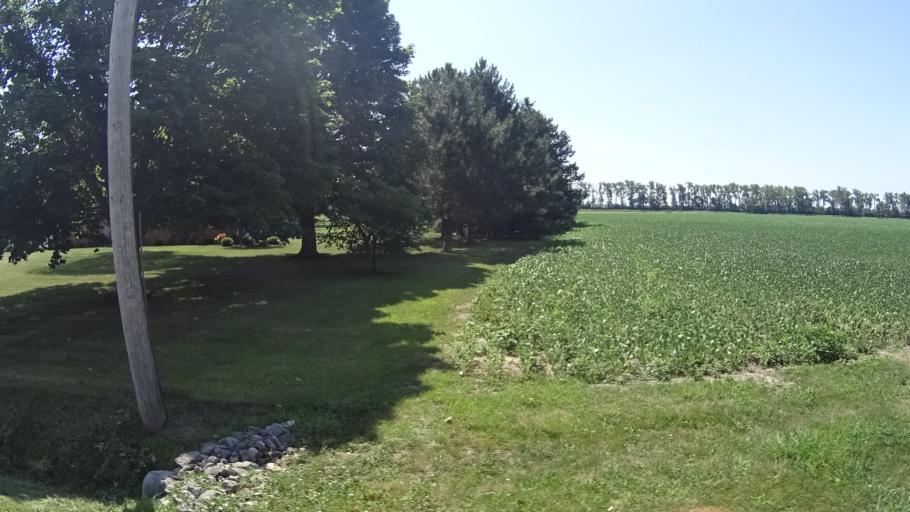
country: US
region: Ohio
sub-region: Erie County
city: Sandusky
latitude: 41.4270
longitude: -82.7971
